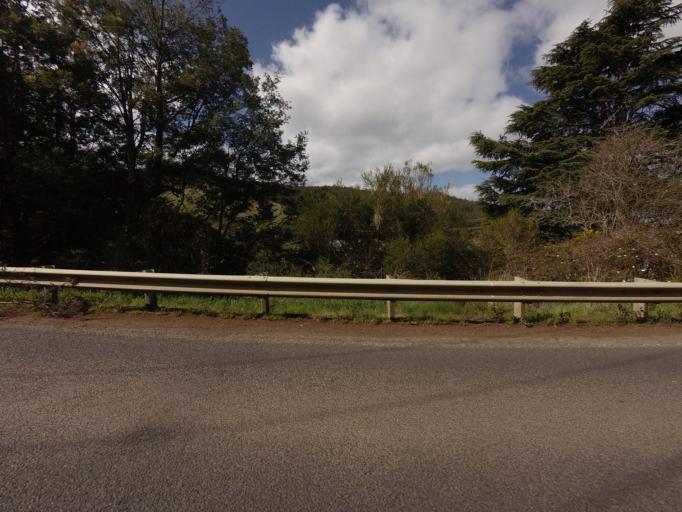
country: AU
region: Tasmania
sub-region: Huon Valley
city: Cygnet
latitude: -43.3075
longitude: 147.0108
